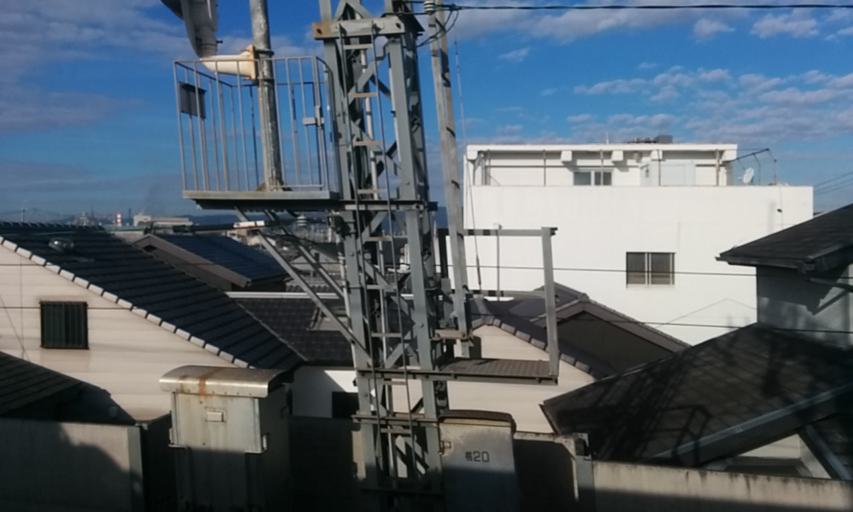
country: JP
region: Kyoto
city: Uji
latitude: 34.9277
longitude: 135.7651
